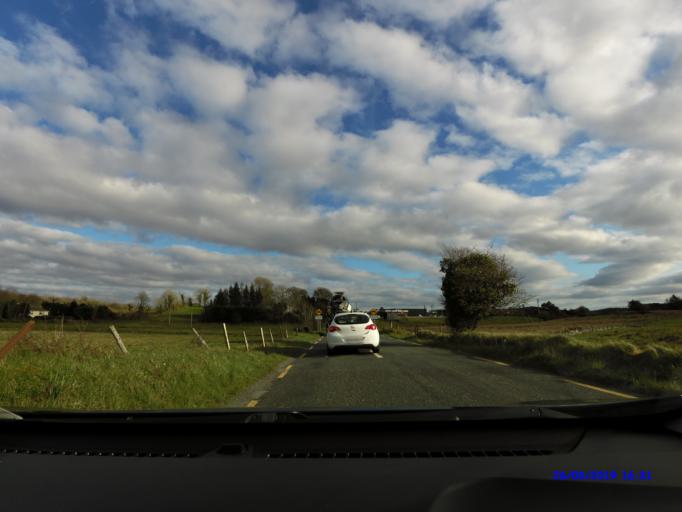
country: IE
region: Connaught
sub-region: Maigh Eo
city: Swinford
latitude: 53.8765
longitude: -8.8575
